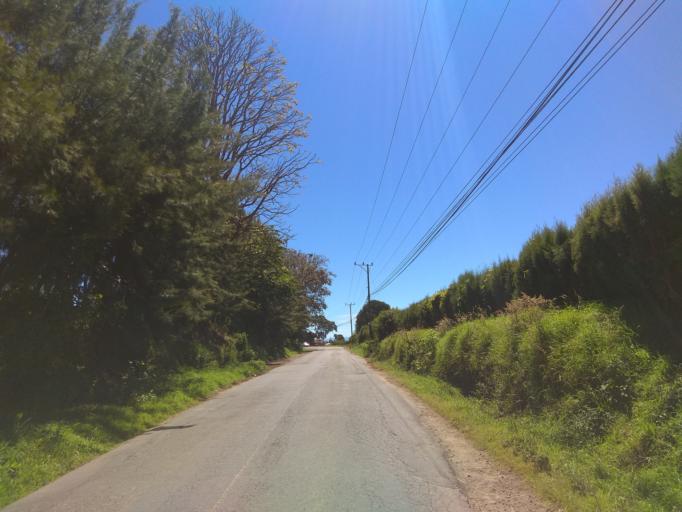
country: CR
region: Cartago
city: Cot
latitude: 9.9439
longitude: -83.9175
